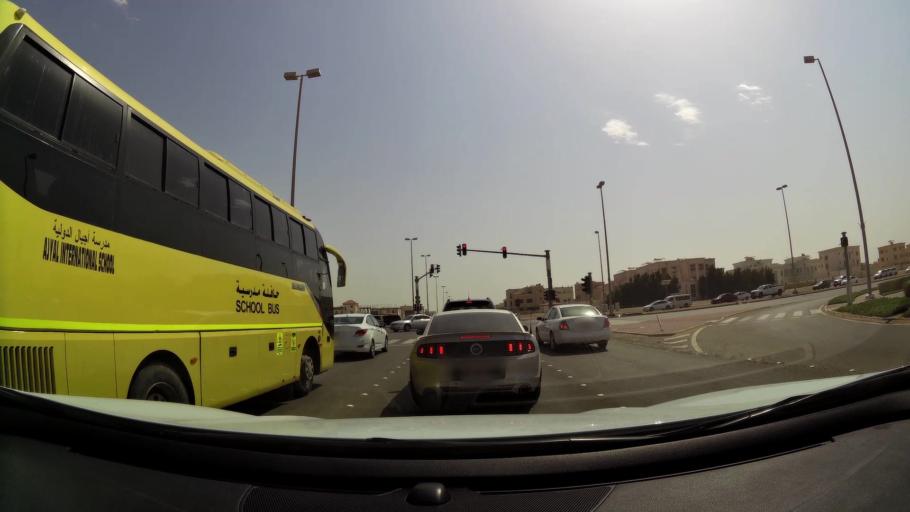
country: AE
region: Abu Dhabi
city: Abu Dhabi
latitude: 24.3255
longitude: 54.5517
